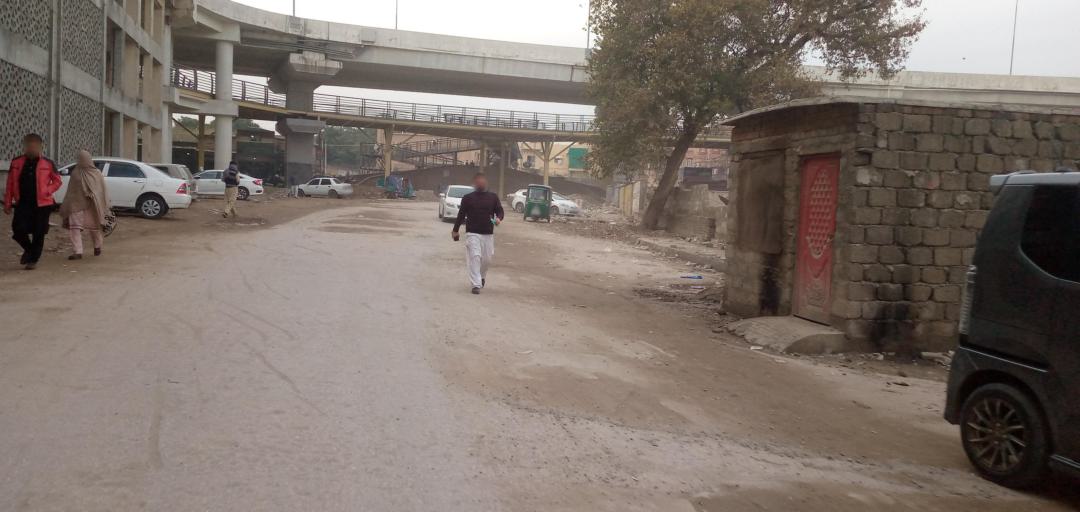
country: PK
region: Khyber Pakhtunkhwa
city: Peshawar
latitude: 34.0058
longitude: 71.5588
